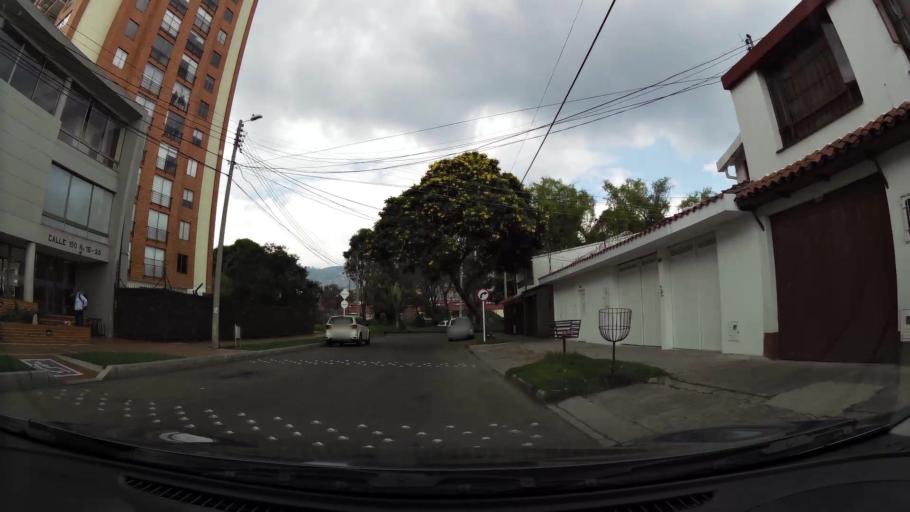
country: CO
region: Bogota D.C.
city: Barrio San Luis
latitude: 4.7313
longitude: -74.0411
